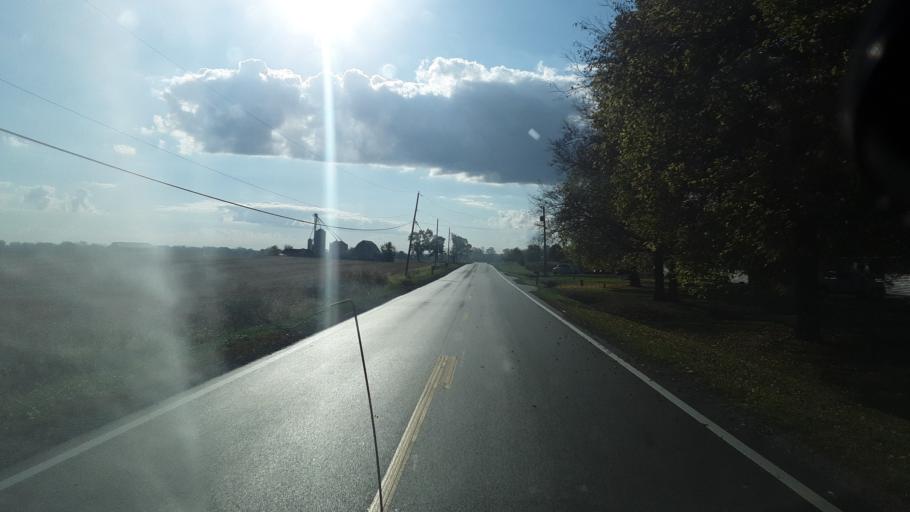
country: US
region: Ohio
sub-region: Fayette County
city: Jeffersonville
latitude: 39.5941
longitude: -83.5122
